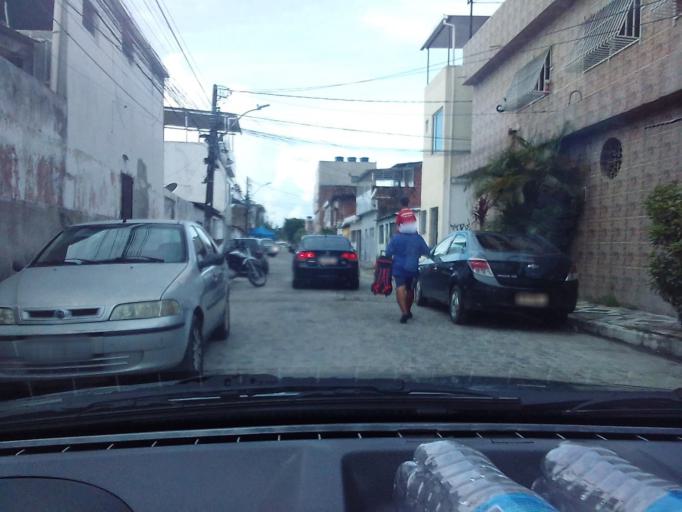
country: BR
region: Pernambuco
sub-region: Recife
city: Recife
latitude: -8.0696
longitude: -34.9275
